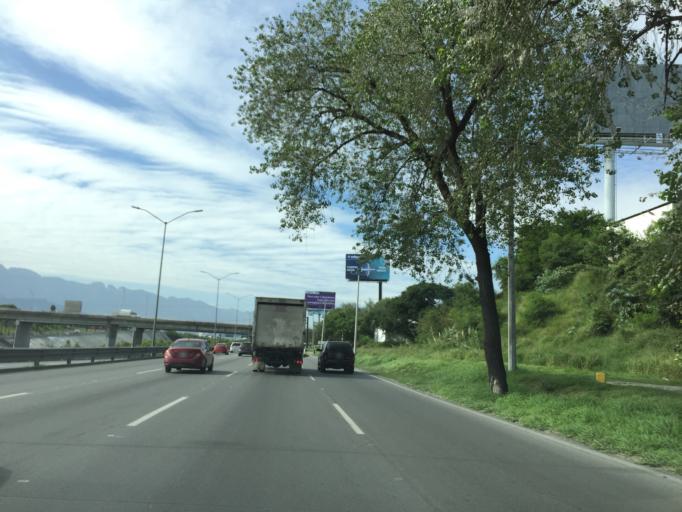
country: MX
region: Nuevo Leon
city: Guadalupe
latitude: 25.6938
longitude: -100.2277
